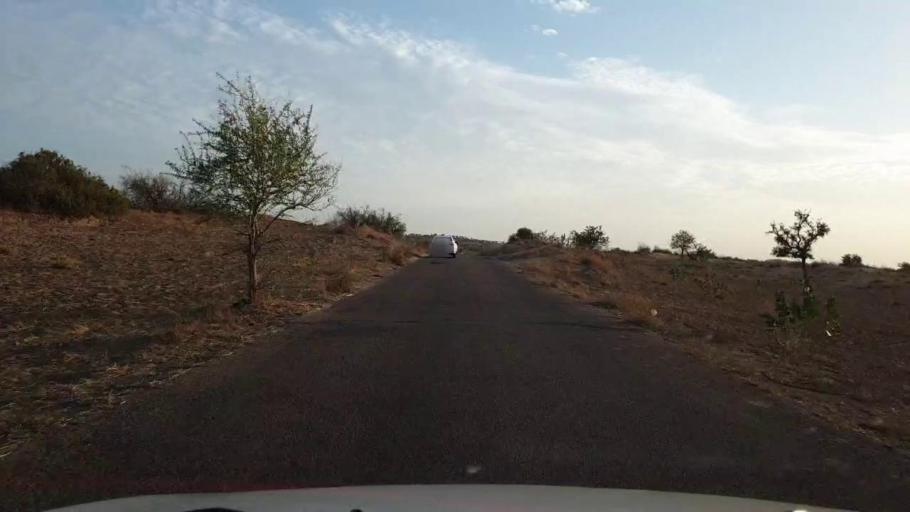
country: PK
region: Sindh
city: Nabisar
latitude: 25.0342
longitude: 69.9511
